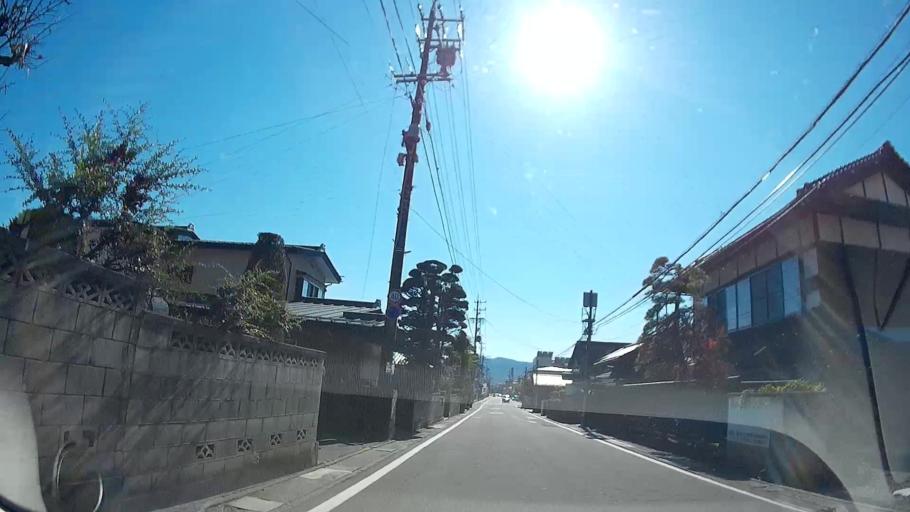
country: JP
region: Nagano
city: Okaya
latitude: 36.0790
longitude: 138.0816
